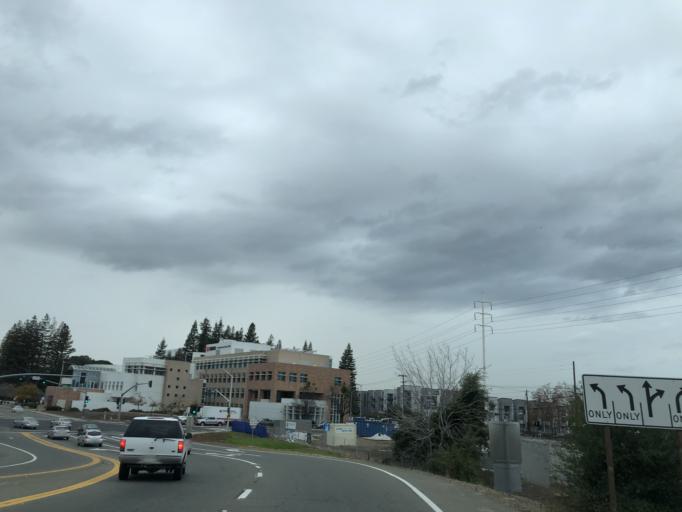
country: US
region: California
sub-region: Sacramento County
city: Florin
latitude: 38.5515
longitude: -121.4266
